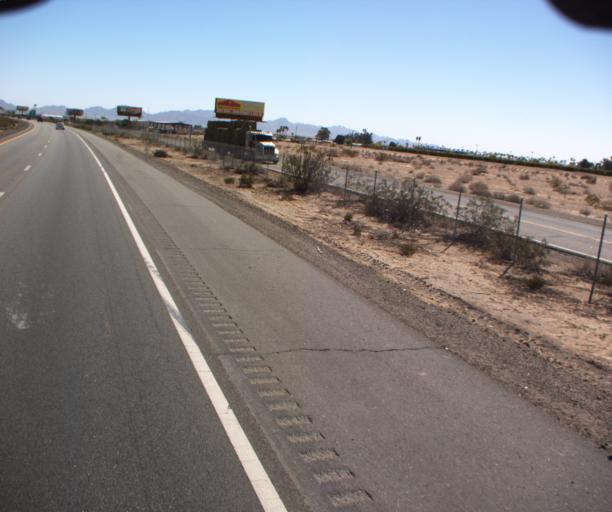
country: US
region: Arizona
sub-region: Yuma County
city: Yuma
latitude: 32.6762
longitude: -114.5401
